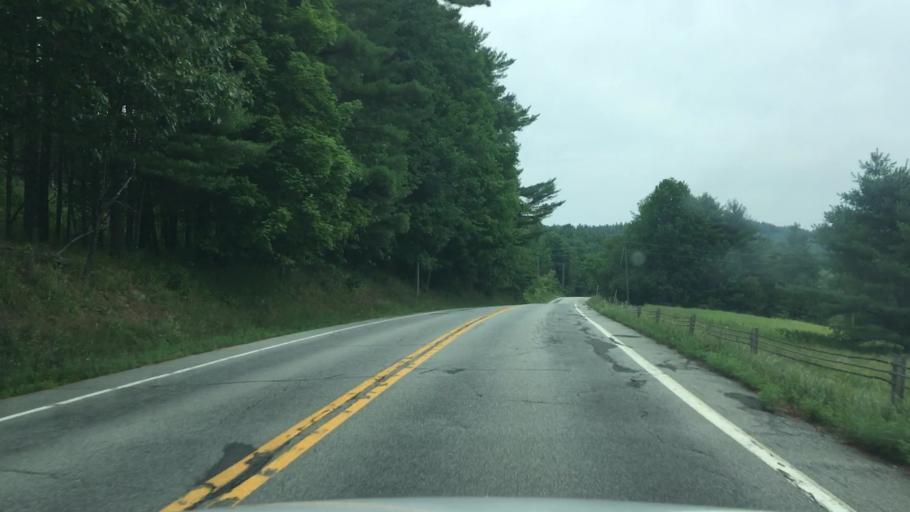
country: US
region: New York
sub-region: Essex County
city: Elizabethtown
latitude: 44.3986
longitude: -73.7078
